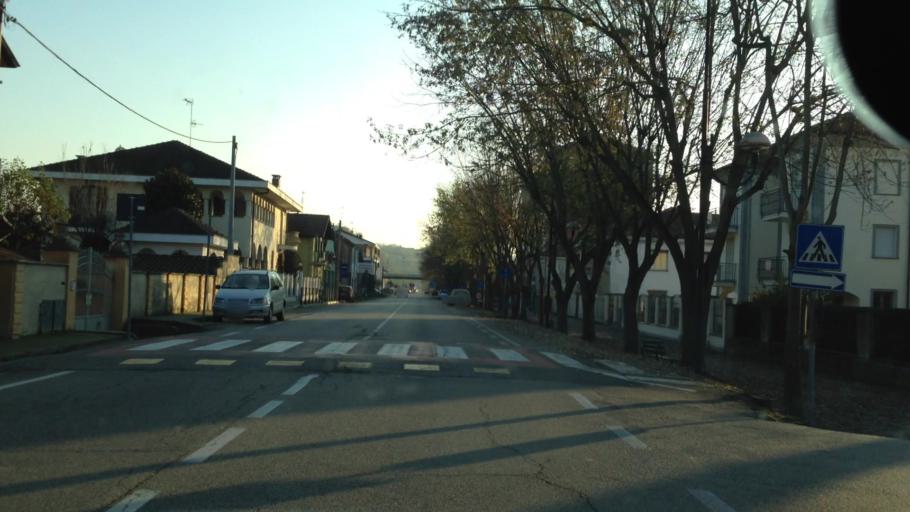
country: IT
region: Piedmont
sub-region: Provincia di Vercelli
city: Crescentino
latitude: 45.1892
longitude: 8.1020
